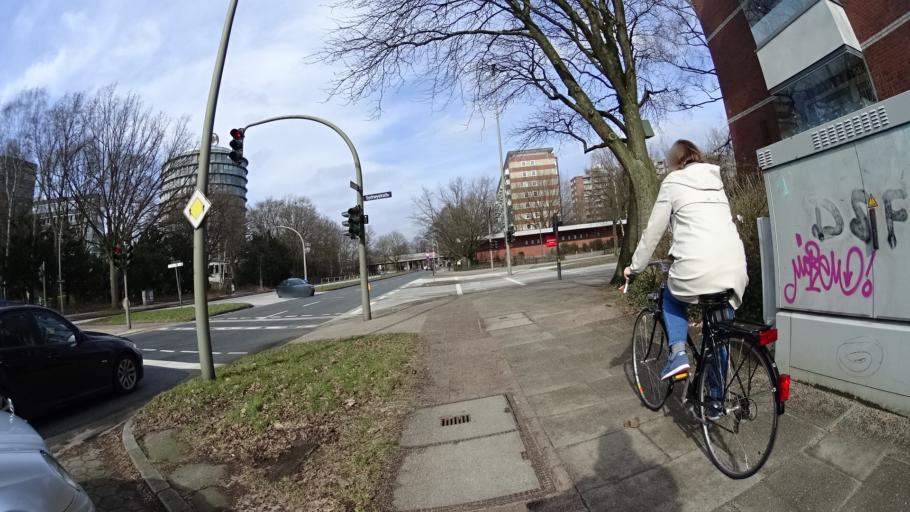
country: DE
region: Hamburg
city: Alsterdorf
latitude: 53.6046
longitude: 10.0130
